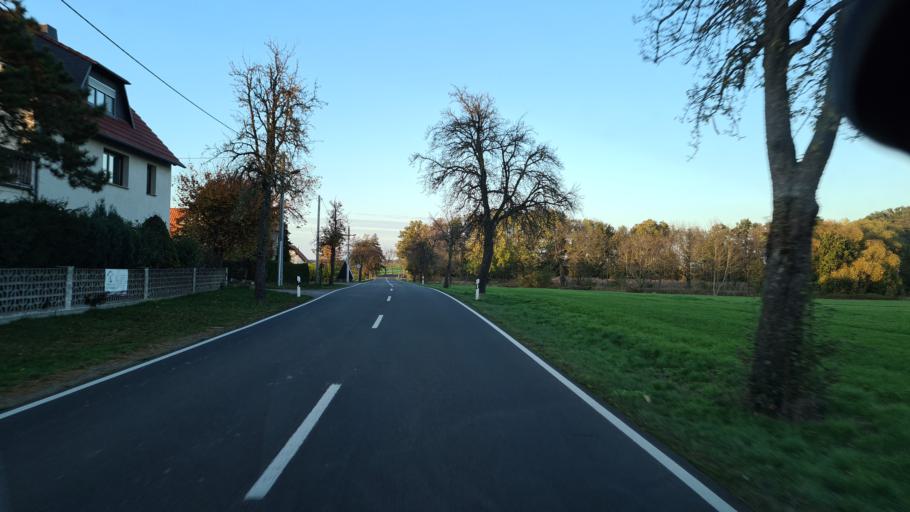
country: DE
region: Saxony
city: Schildau
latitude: 51.4543
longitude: 12.9721
